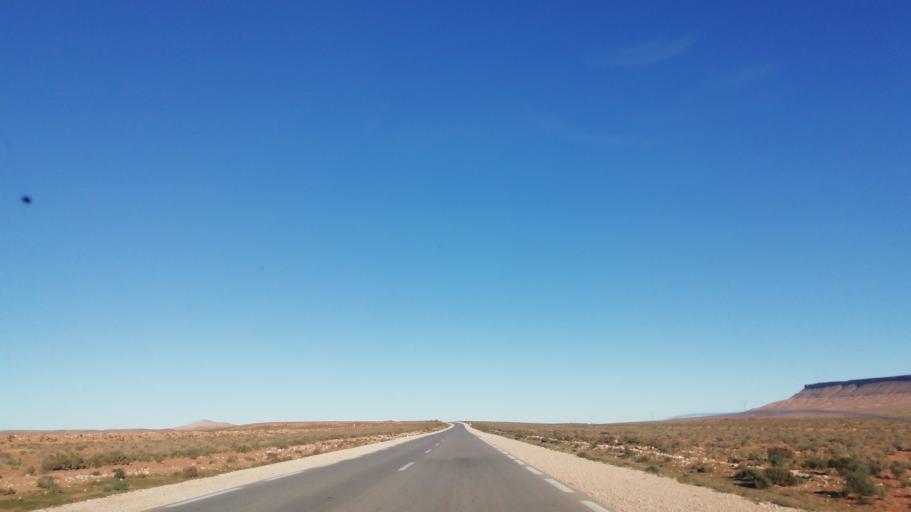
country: DZ
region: El Bayadh
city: El Abiodh Sidi Cheikh
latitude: 33.0922
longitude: 0.1951
